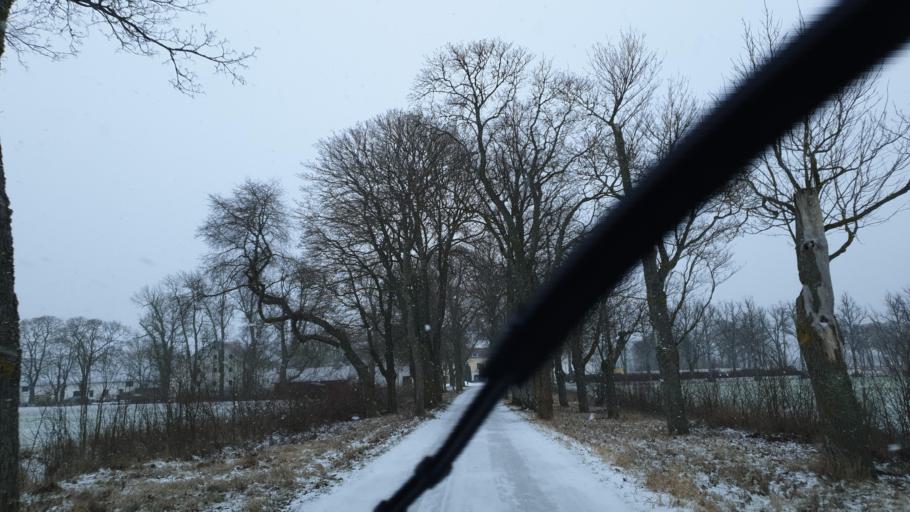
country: SE
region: Gotland
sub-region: Gotland
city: Visby
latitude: 57.5175
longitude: 18.4571
